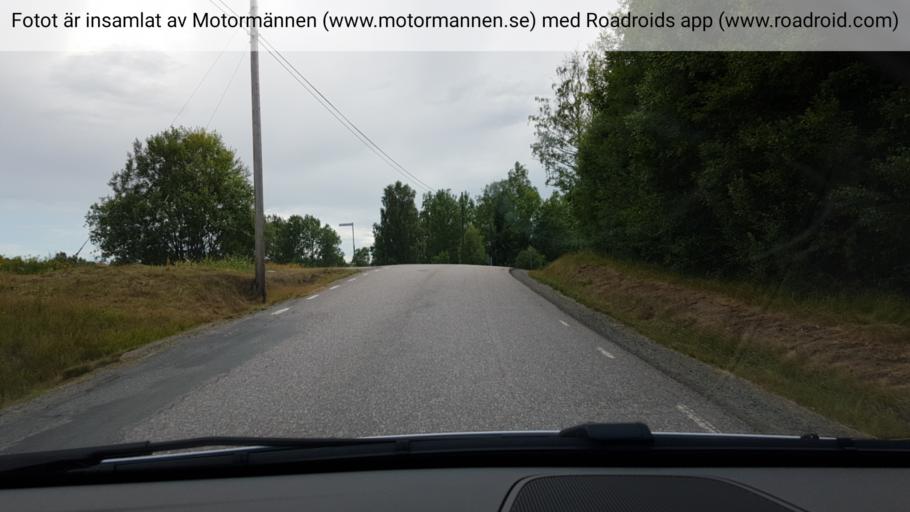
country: SE
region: Stockholm
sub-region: Nynashamns Kommun
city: Osmo
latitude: 59.0810
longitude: 17.8879
